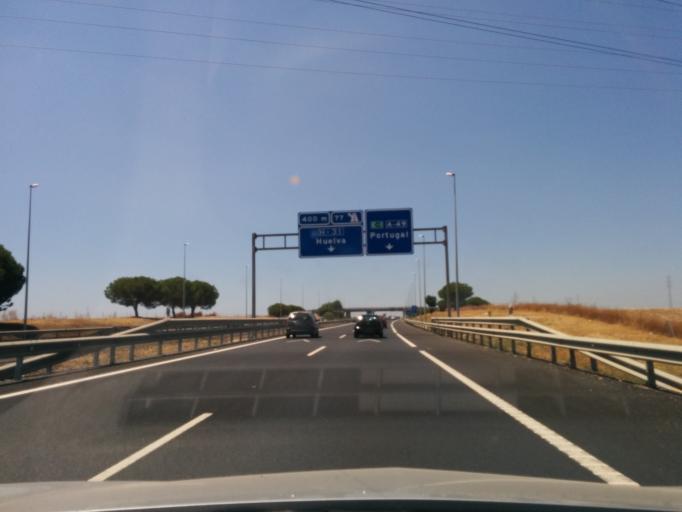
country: ES
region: Andalusia
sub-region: Provincia de Huelva
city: San Juan del Puerto
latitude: 37.3166
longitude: -6.8623
